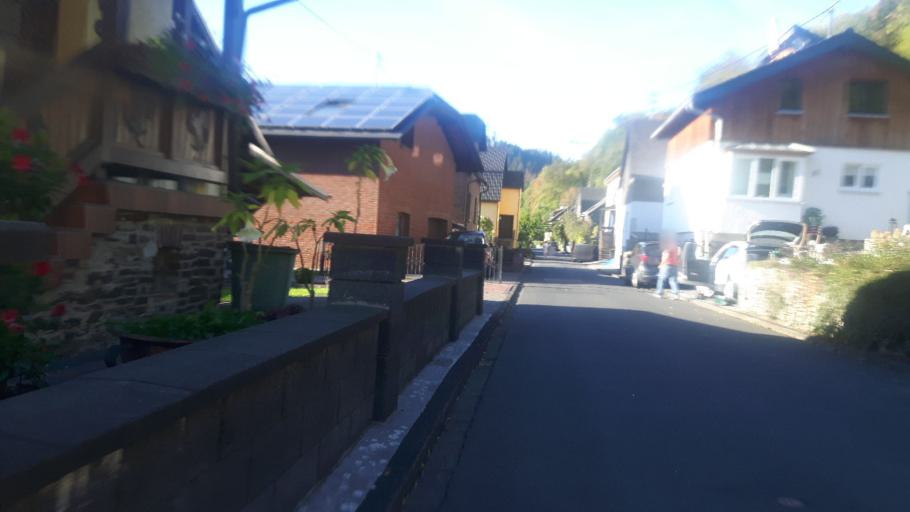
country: DE
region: Rheinland-Pfalz
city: Kirchen
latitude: 50.8175
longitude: 7.8848
